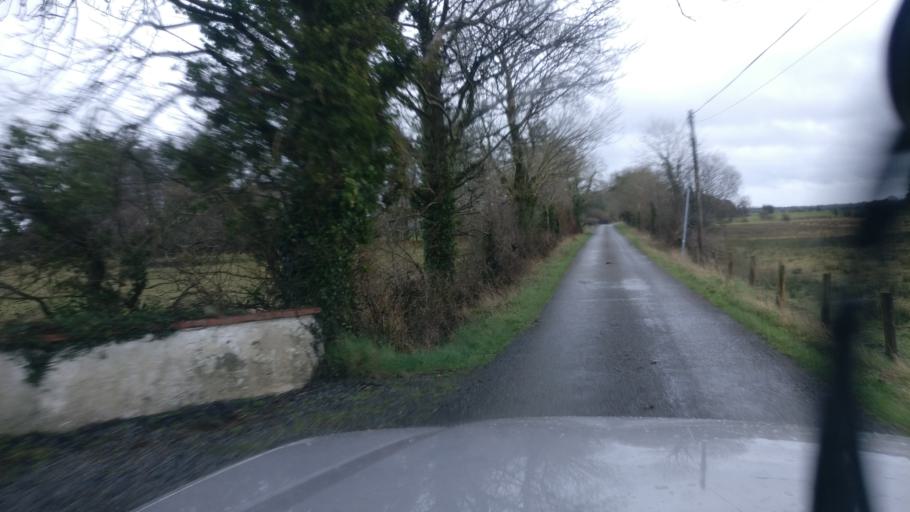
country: IE
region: Connaught
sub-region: County Galway
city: Ballinasloe
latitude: 53.2597
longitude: -8.3543
